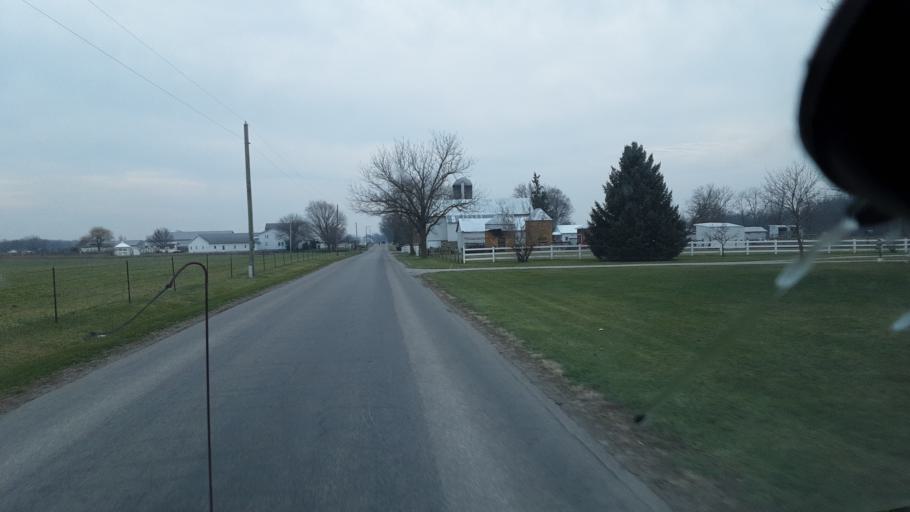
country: US
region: Indiana
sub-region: Elkhart County
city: Middlebury
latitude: 41.6960
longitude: -85.6200
